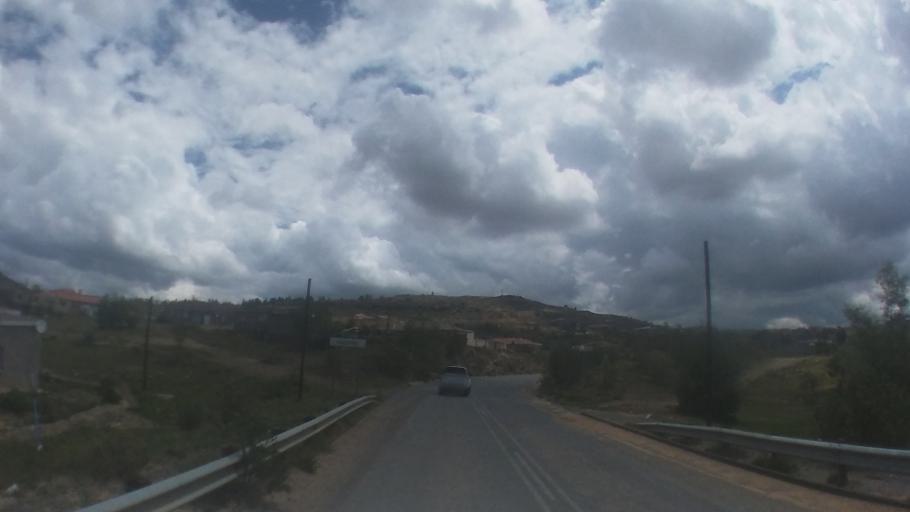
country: LS
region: Maseru
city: Maseru
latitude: -29.4002
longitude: 27.4743
